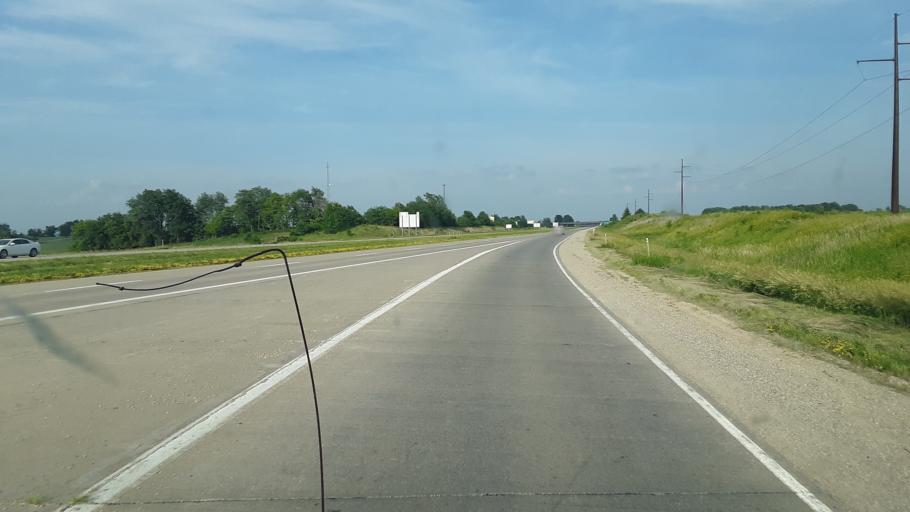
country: US
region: Iowa
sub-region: Marshall County
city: Marshalltown
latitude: 42.0034
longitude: -92.9078
